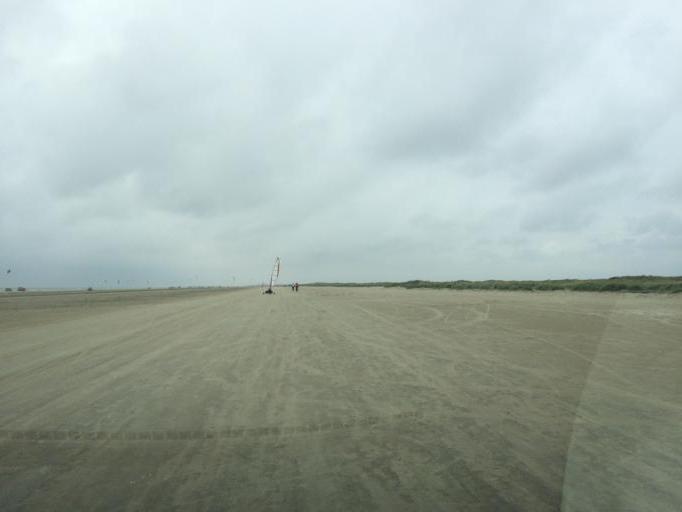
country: DK
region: South Denmark
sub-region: Fano Kommune
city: Nordby
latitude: 55.3891
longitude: 8.4003
